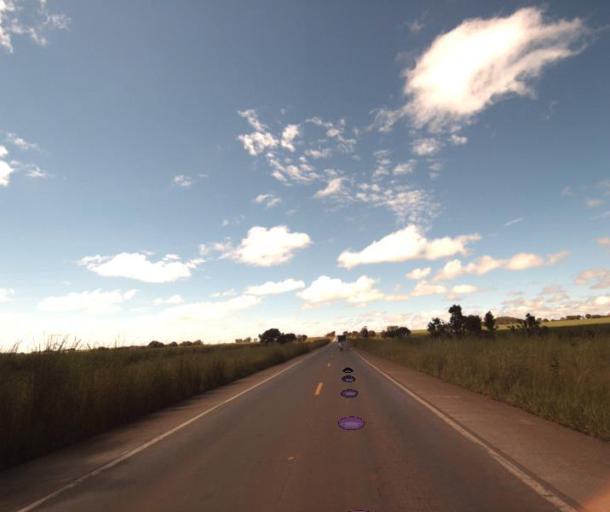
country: BR
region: Goias
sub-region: Rialma
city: Rialma
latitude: -15.4149
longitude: -49.5239
